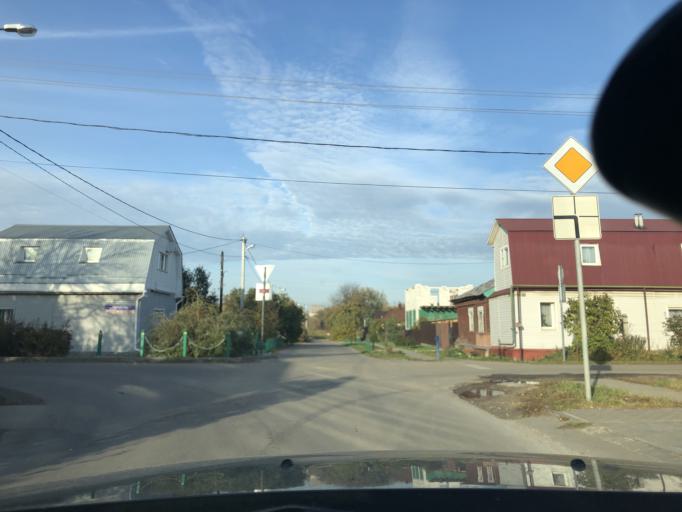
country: RU
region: Tula
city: Tula
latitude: 54.1873
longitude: 37.6370
